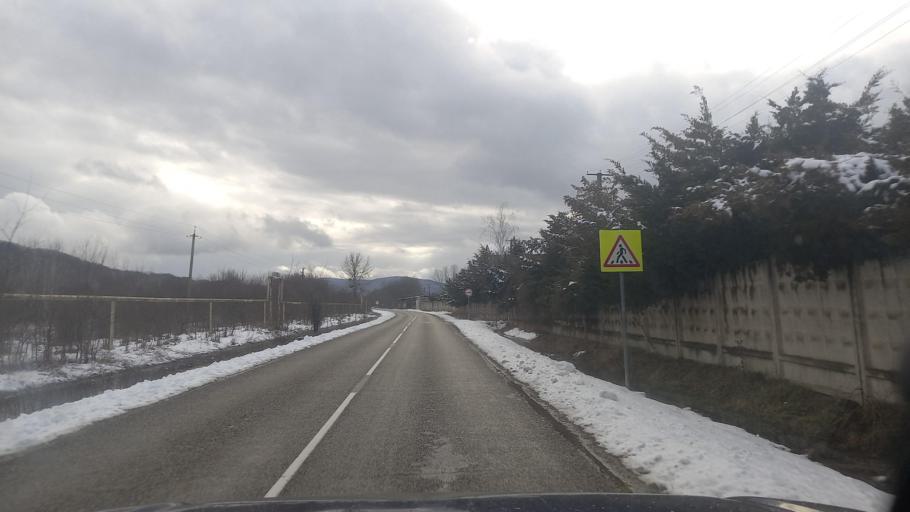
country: RU
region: Krasnodarskiy
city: Smolenskaya
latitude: 44.7506
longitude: 38.8416
